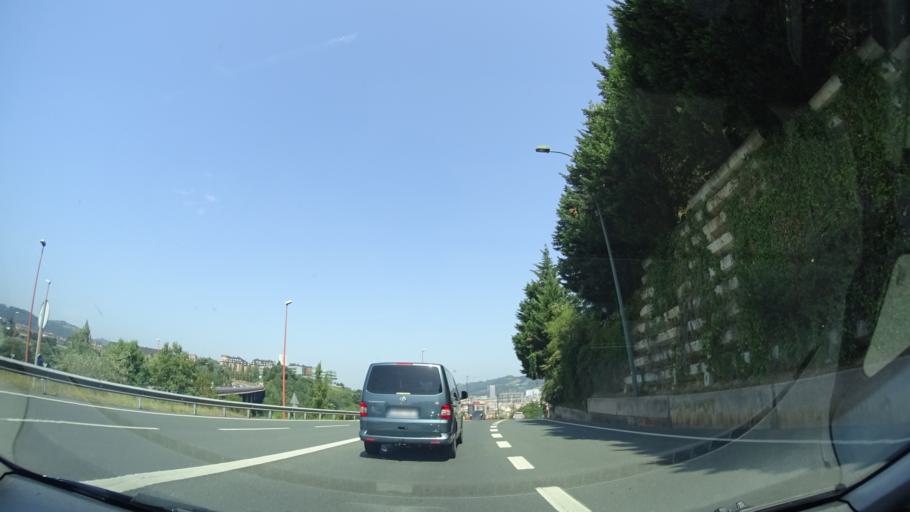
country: ES
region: Basque Country
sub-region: Bizkaia
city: Santutxu
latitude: 43.2461
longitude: -2.9189
